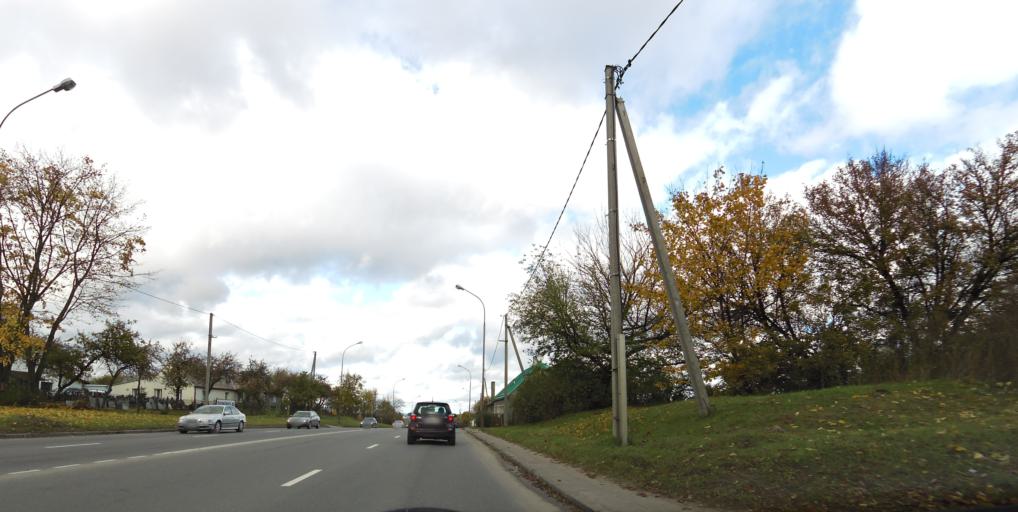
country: LT
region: Vilnius County
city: Rasos
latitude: 54.6557
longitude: 25.3030
